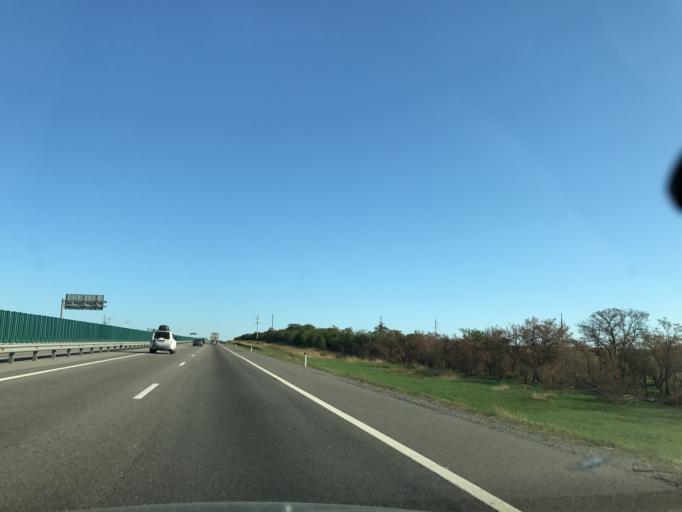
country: RU
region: Rostov
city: Glubokiy
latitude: 48.5427
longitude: 40.3470
